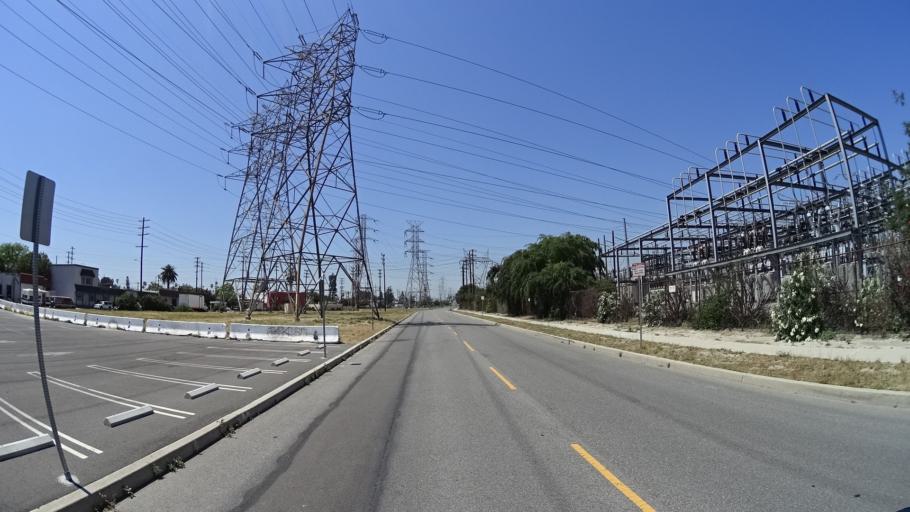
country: US
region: California
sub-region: Los Angeles County
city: North Hollywood
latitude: 34.1741
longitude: -118.3591
